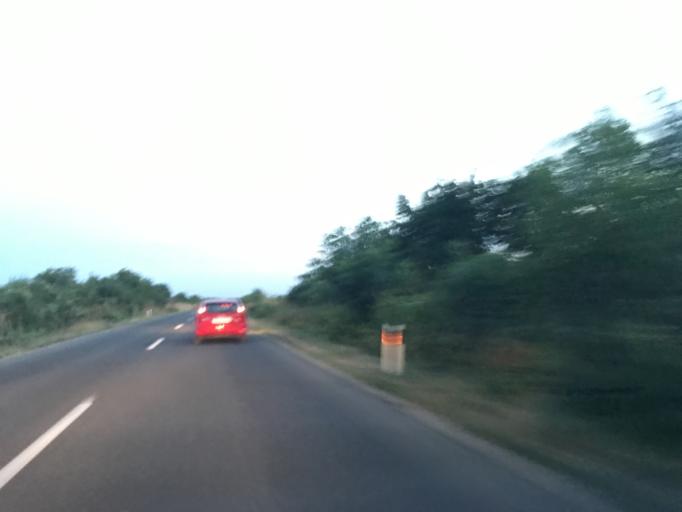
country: RS
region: Central Serbia
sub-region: Branicevski Okrug
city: Pozarevac
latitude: 44.6188
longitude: 21.1461
